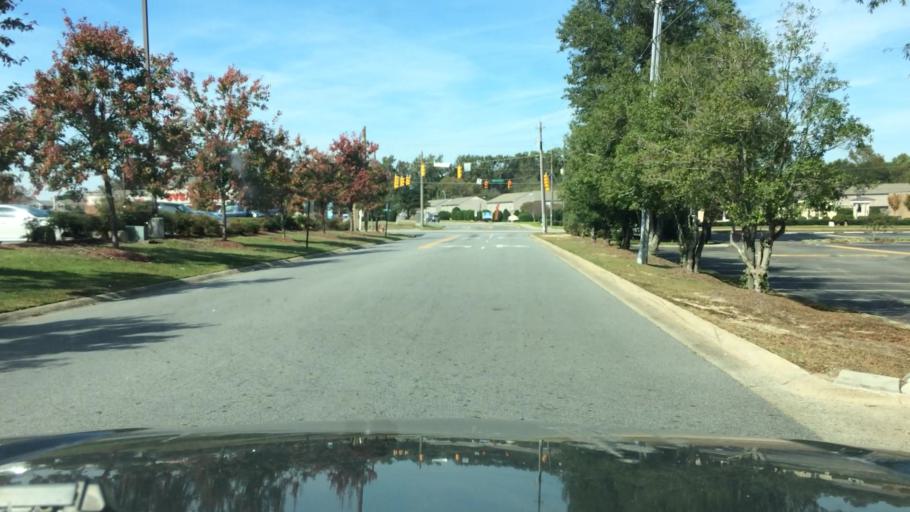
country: US
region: North Carolina
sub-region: Wayne County
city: Goldsboro
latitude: 35.3974
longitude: -77.9617
